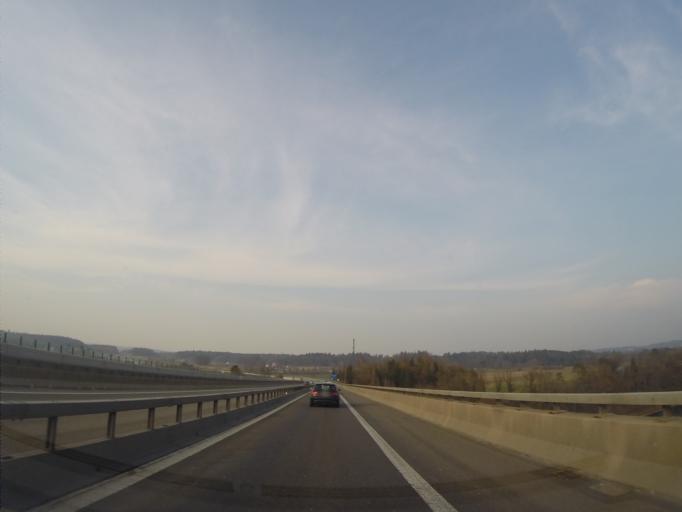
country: CH
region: Zurich
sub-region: Bezirk Andelfingen
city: Kleinandelfingen
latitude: 47.5964
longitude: 8.6901
